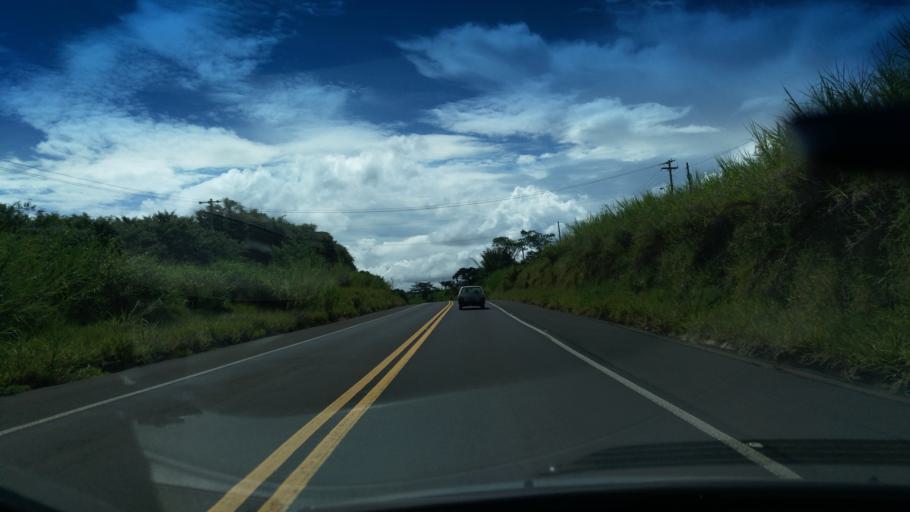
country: BR
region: Sao Paulo
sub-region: Santo Antonio Do Jardim
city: Espirito Santo do Pinhal
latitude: -22.1617
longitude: -46.7321
